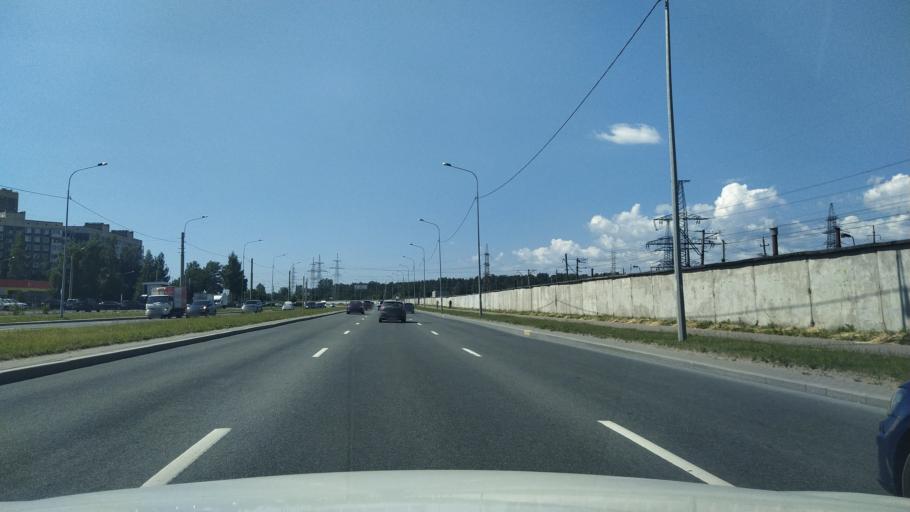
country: RU
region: St.-Petersburg
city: Shuvalovo
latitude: 60.0667
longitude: 30.3127
